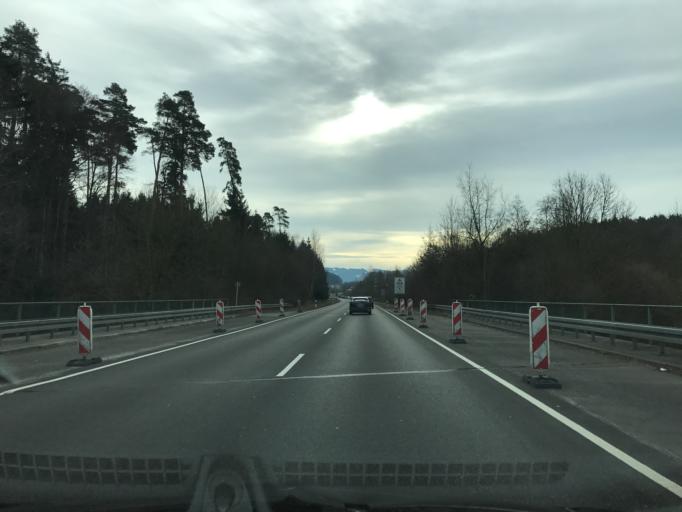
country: DE
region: Bavaria
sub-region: Swabia
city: Bodolz
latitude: 47.5901
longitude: 9.6471
